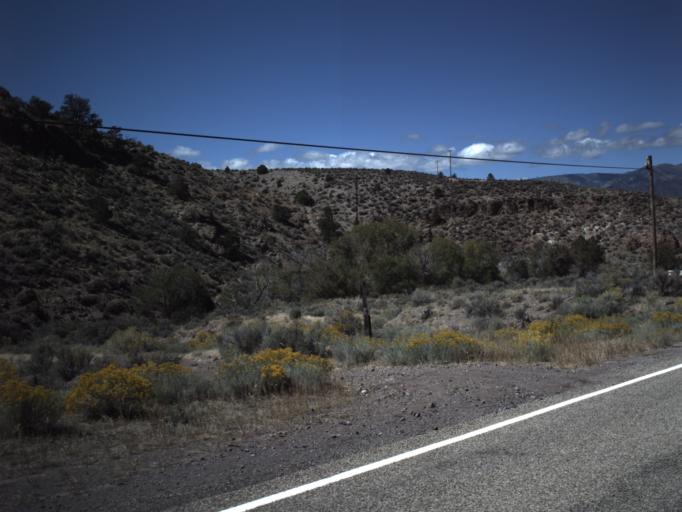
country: US
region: Utah
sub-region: Piute County
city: Junction
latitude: 38.1990
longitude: -112.1518
